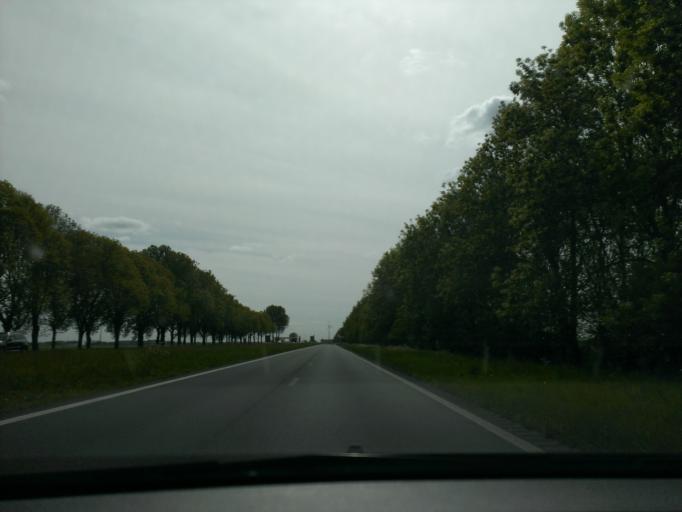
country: NL
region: Gelderland
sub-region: Gemeente Harderwijk
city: Harderwijk
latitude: 52.4040
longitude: 5.5898
